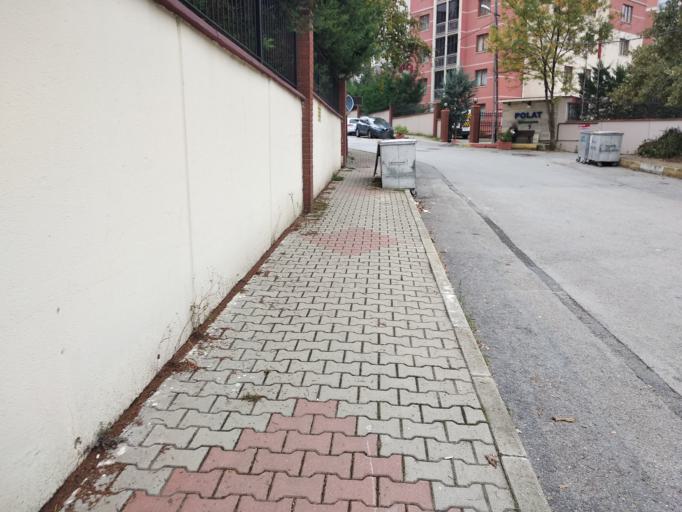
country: TR
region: Istanbul
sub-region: Atasehir
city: Atasehir
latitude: 40.9804
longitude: 29.1226
